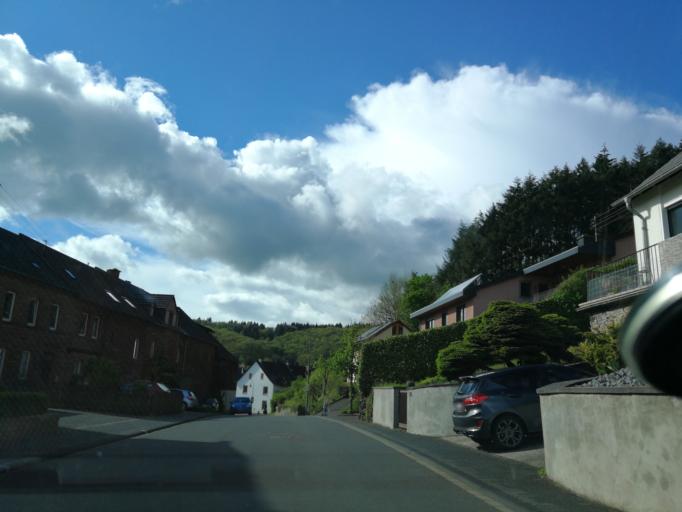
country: DE
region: Rheinland-Pfalz
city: Wittlich
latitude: 50.0007
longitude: 6.9068
